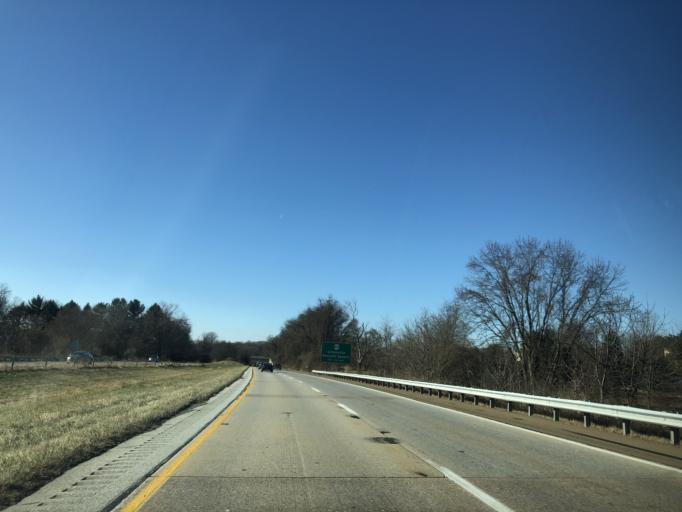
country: US
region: Pennsylvania
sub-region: Chester County
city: Kennett Square
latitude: 39.8576
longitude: -75.6988
